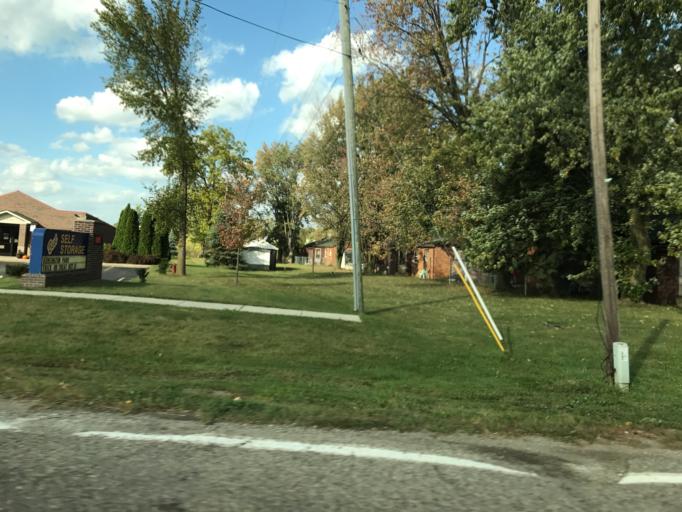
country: US
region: Michigan
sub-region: Oakland County
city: Wixom
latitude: 42.5045
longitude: -83.5822
